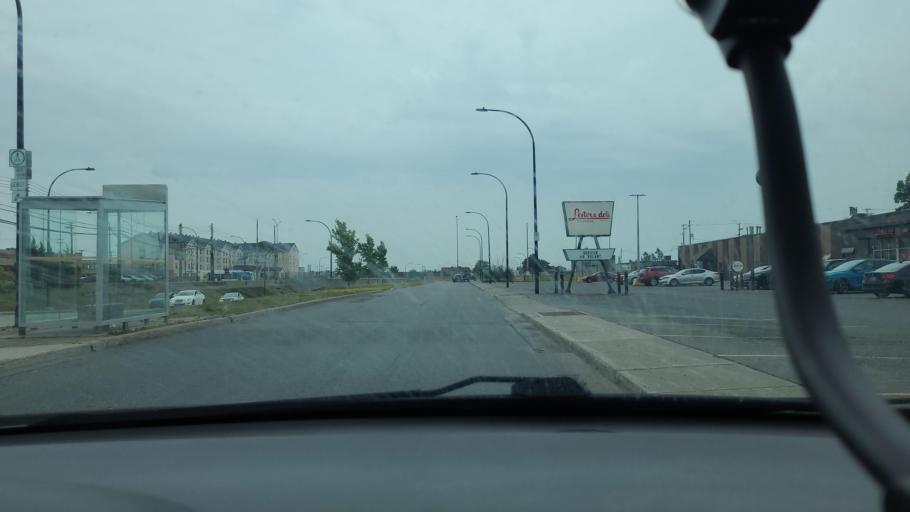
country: CA
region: Quebec
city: Cote-Saint-Luc
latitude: 45.4781
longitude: -73.7050
